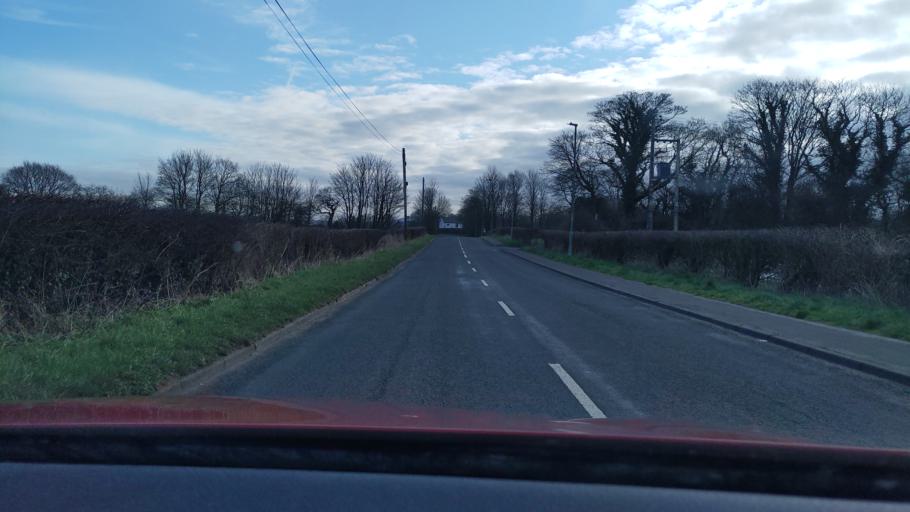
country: GB
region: England
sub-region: Lancashire
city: Coppull
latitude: 53.6105
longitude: -2.6641
